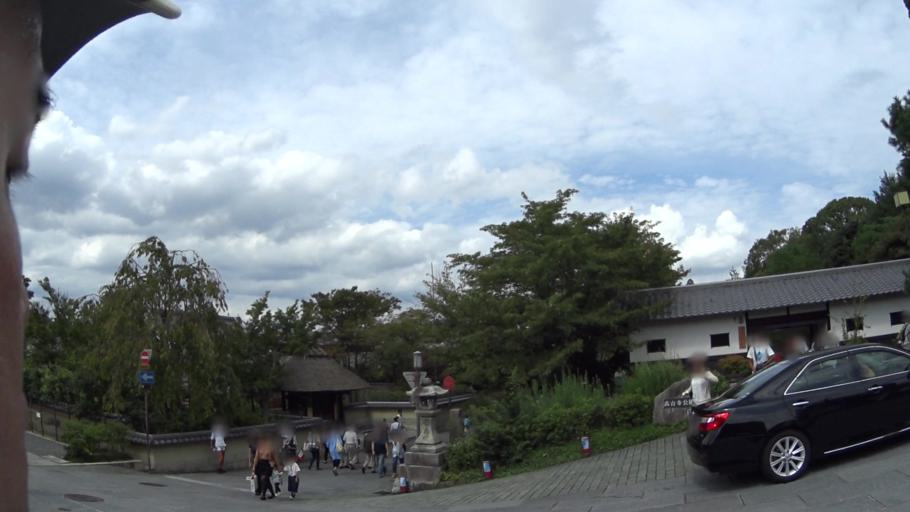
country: JP
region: Kyoto
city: Kyoto
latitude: 34.9993
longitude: 135.7800
